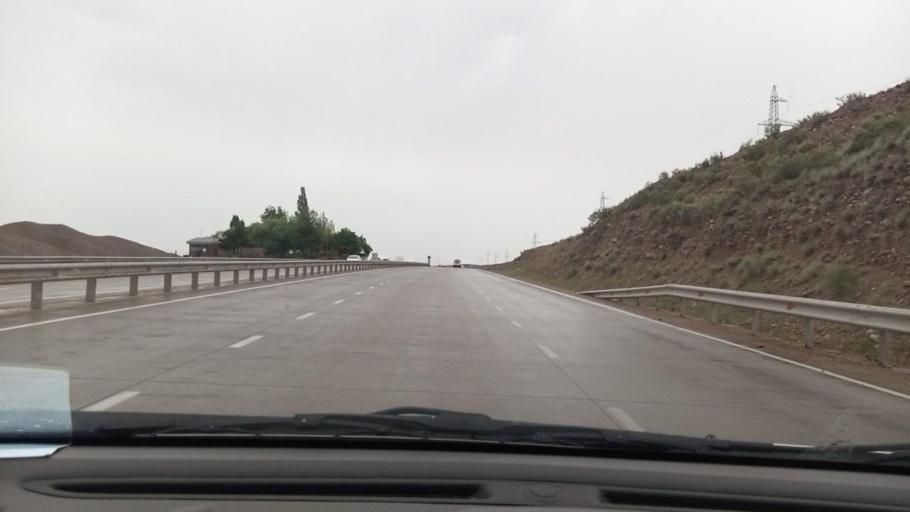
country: UZ
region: Namangan
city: Pop Shahri
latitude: 40.9421
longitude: 70.6884
